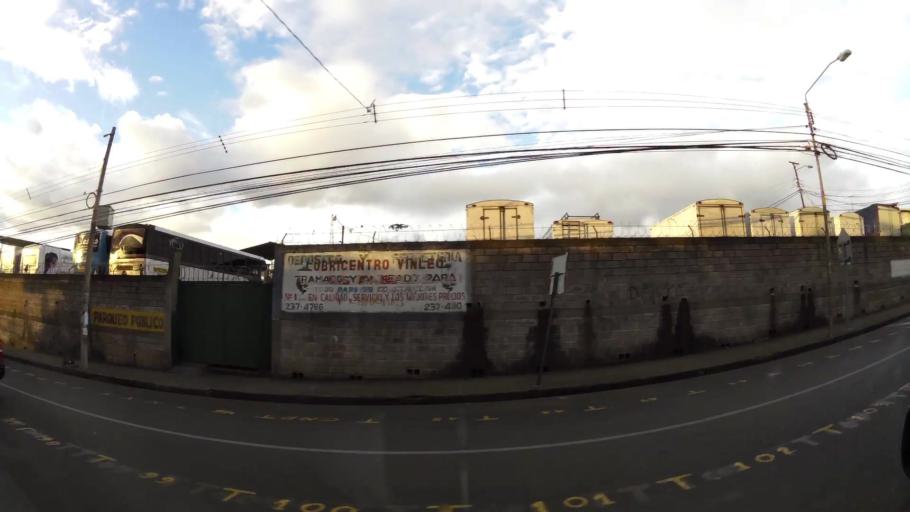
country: CR
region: Heredia
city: San Francisco
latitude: 9.9934
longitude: -84.1204
